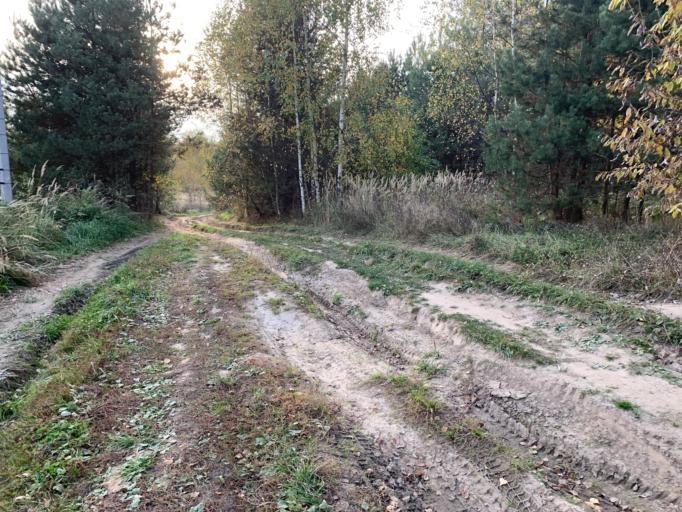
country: RU
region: Jaroslavl
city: Petrovsk
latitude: 56.9817
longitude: 39.3755
